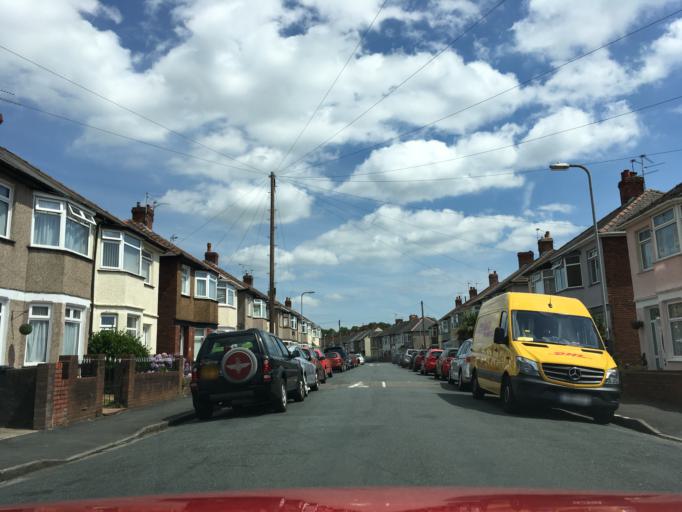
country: GB
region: Wales
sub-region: Newport
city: Caerleon
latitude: 51.5867
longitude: -2.9677
